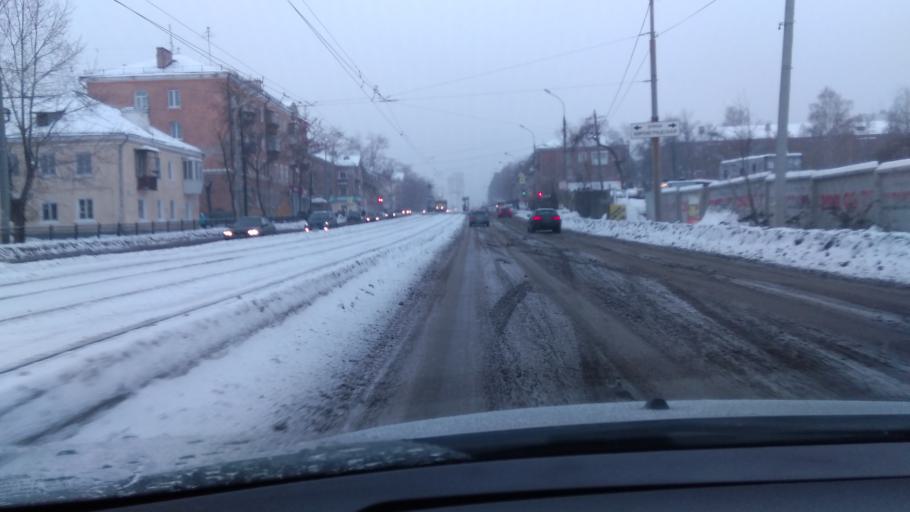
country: RU
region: Sverdlovsk
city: Yekaterinburg
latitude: 56.8990
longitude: 60.5796
